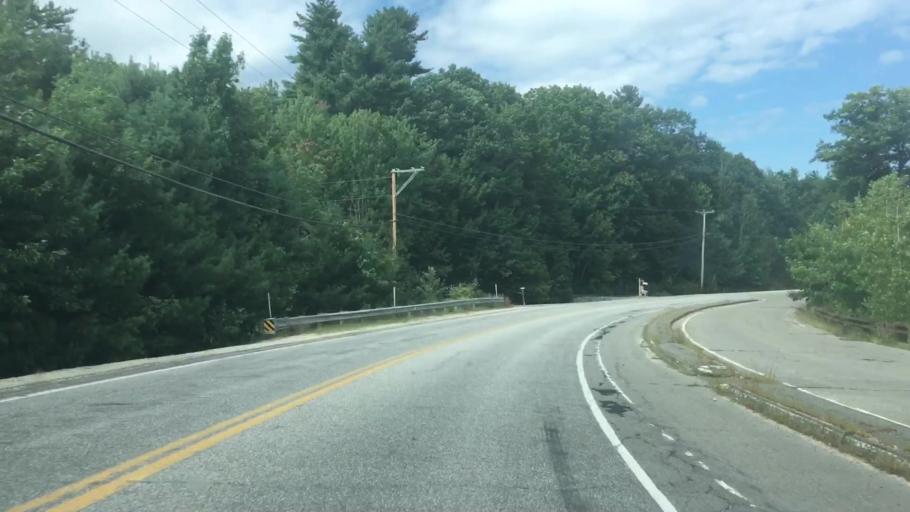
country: US
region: Maine
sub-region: Cumberland County
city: Raymond
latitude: 43.9894
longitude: -70.5209
